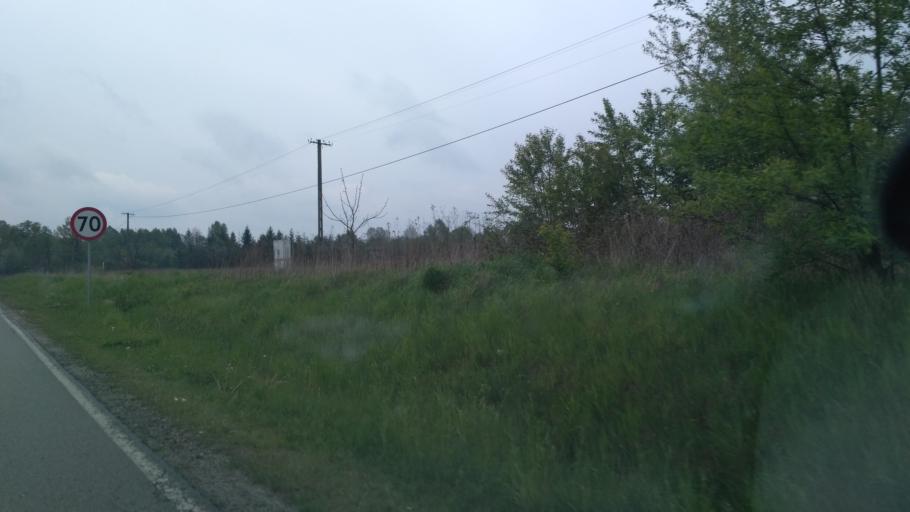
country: PL
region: Subcarpathian Voivodeship
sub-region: Powiat ropczycko-sedziszowski
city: Sedziszow Malopolski
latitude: 50.0915
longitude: 21.7291
